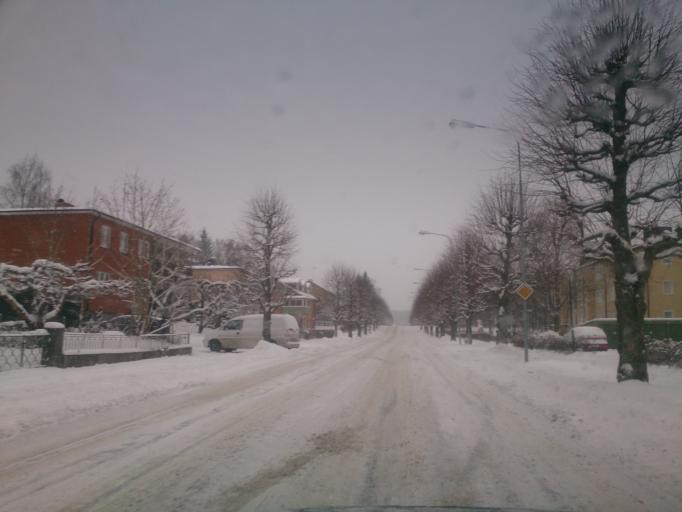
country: SE
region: OEstergoetland
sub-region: Finspangs Kommun
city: Finspang
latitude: 58.7079
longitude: 15.7910
